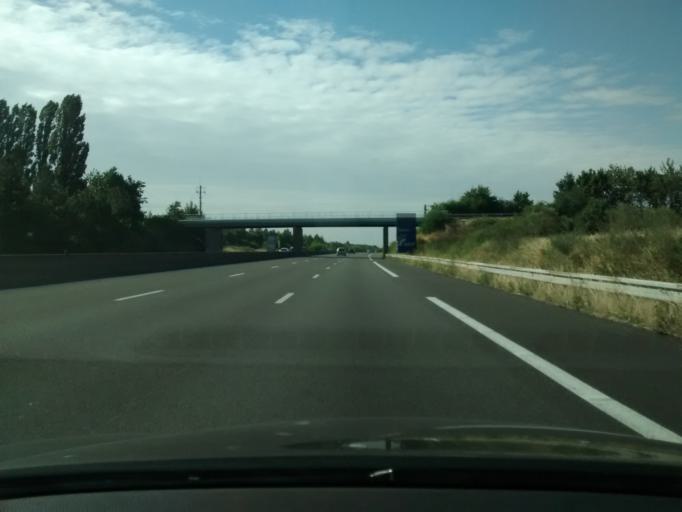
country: FR
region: Ile-de-France
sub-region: Departement des Yvelines
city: Saint-Arnoult-en-Yvelines
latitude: 48.5245
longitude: 1.9076
